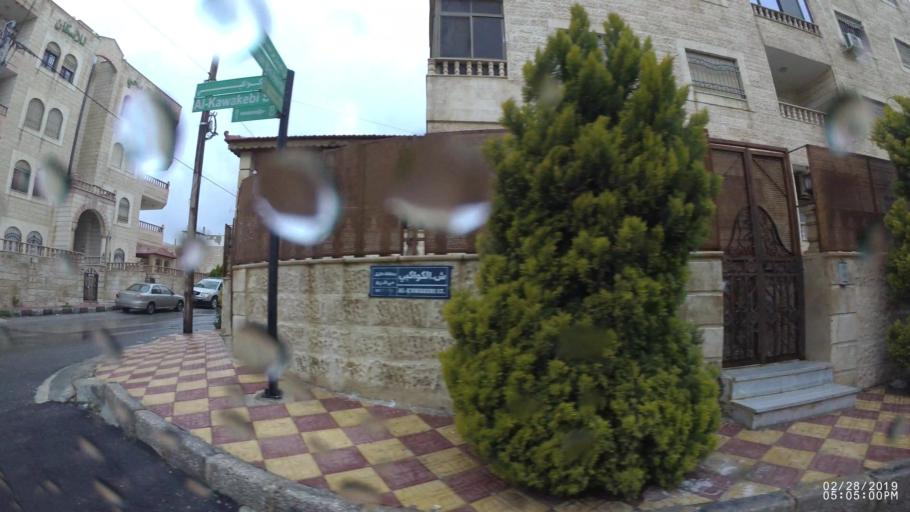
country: JO
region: Amman
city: Amman
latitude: 31.9974
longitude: 35.9284
